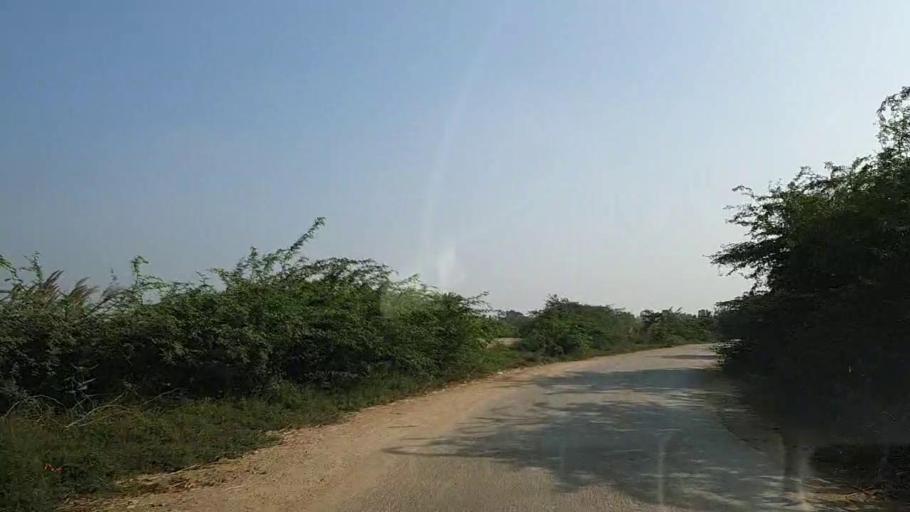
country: PK
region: Sindh
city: Mirpur Sakro
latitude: 24.6203
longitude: 67.6594
